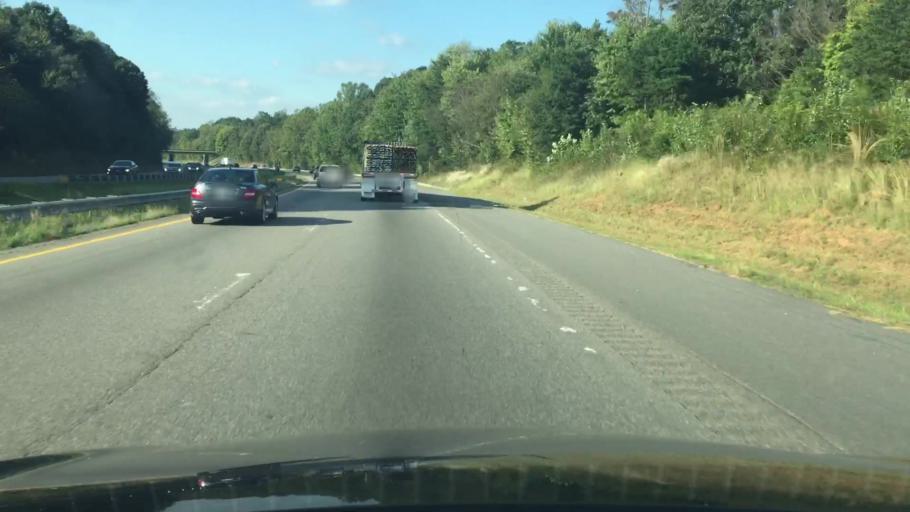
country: US
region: North Carolina
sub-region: Iredell County
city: Troutman
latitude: 35.6841
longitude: -80.8526
